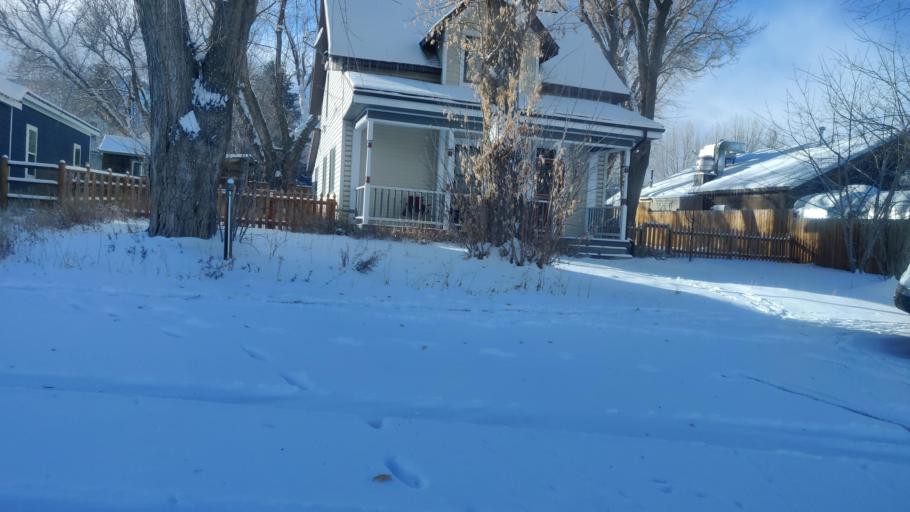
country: US
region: Colorado
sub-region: Ouray County
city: Ouray
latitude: 38.1510
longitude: -107.7564
